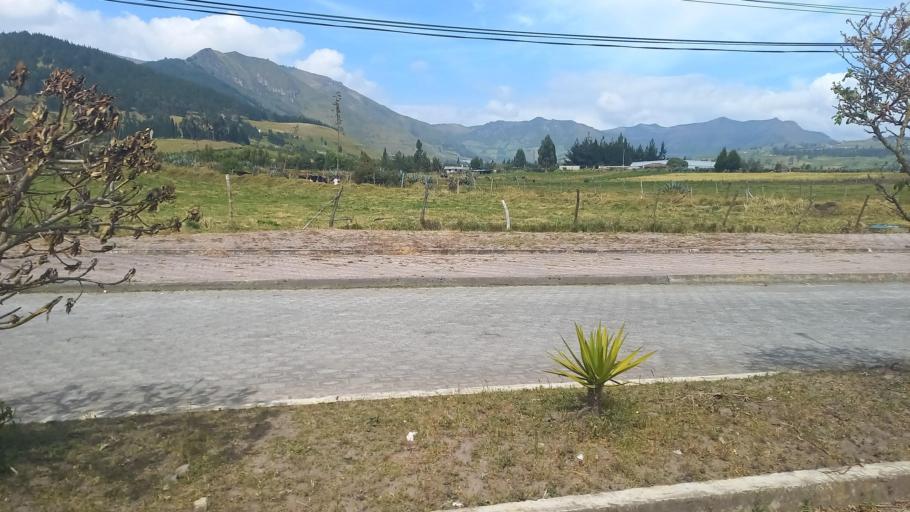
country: EC
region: Pichincha
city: Cayambe
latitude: 0.1443
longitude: -78.0706
